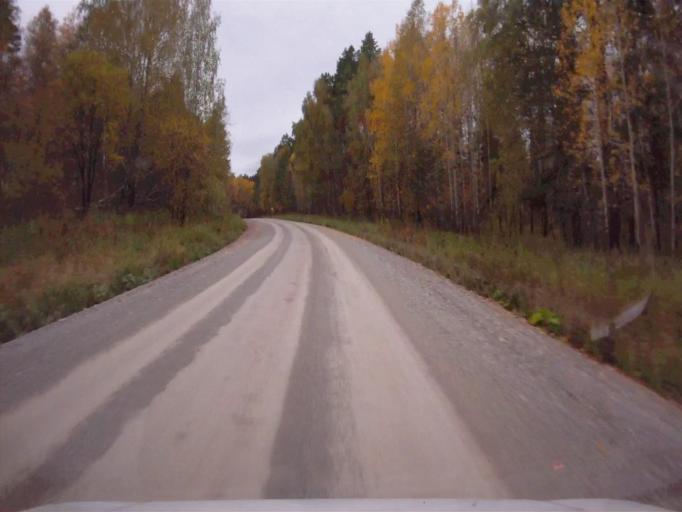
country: RU
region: Chelyabinsk
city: Nyazepetrovsk
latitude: 56.0664
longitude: 59.4382
